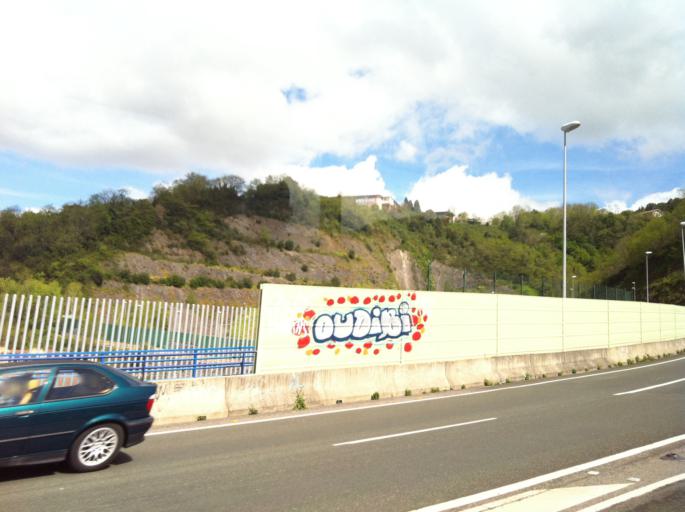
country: ES
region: Basque Country
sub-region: Bizkaia
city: Bilbao
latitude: 43.2697
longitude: -2.9315
